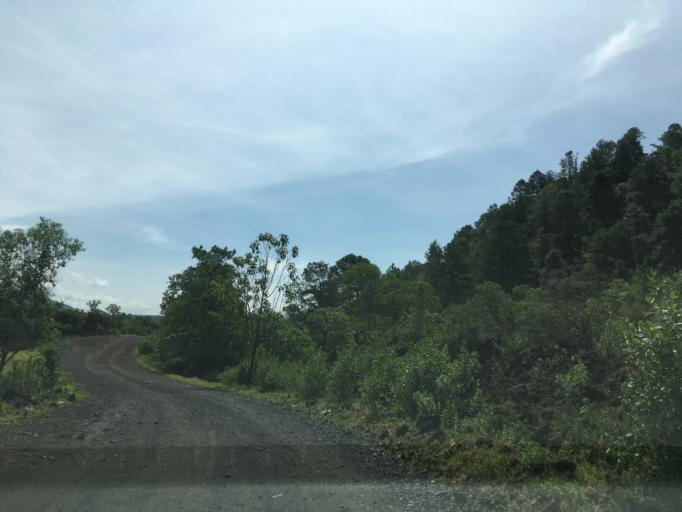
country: MX
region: Michoacan
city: Angahuan
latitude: 19.5273
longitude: -102.2421
